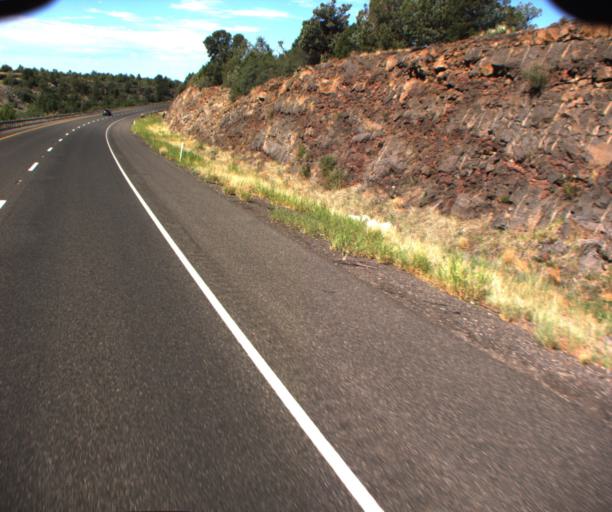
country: US
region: Arizona
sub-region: Yavapai County
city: Village of Oak Creek (Big Park)
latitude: 34.7714
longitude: -111.6407
